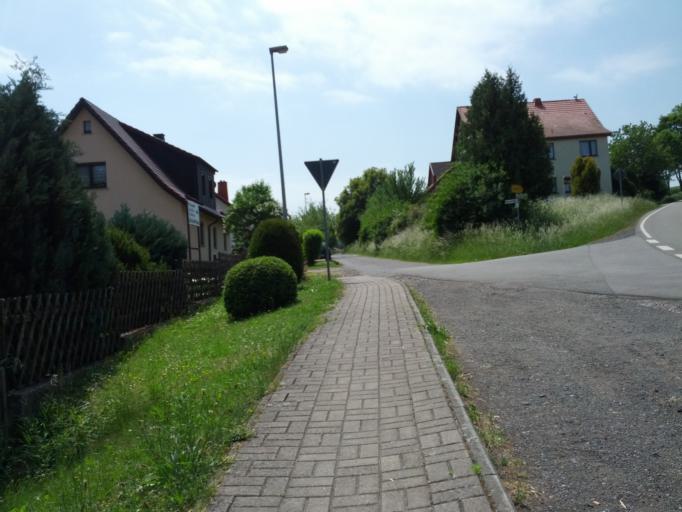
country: DE
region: Thuringia
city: Urnshausen
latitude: 50.7345
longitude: 10.1703
